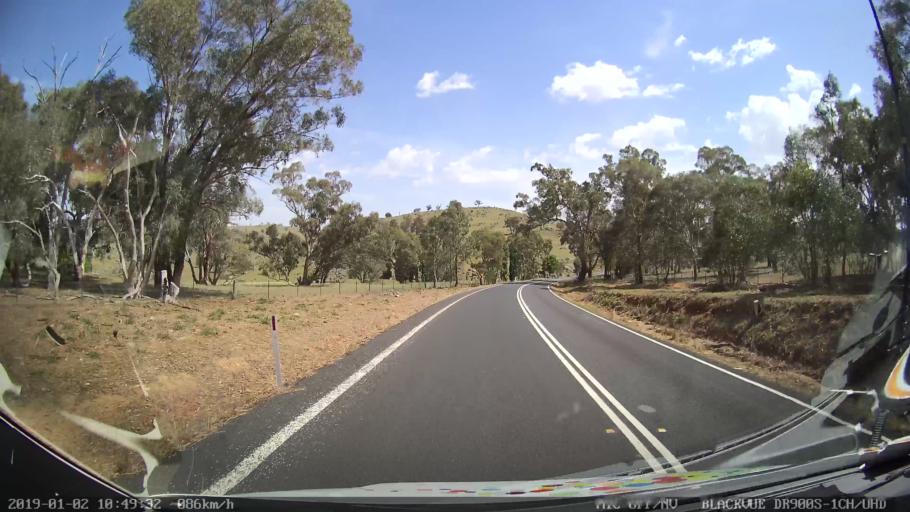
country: AU
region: New South Wales
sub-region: Cootamundra
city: Cootamundra
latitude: -34.7229
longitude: 148.2760
